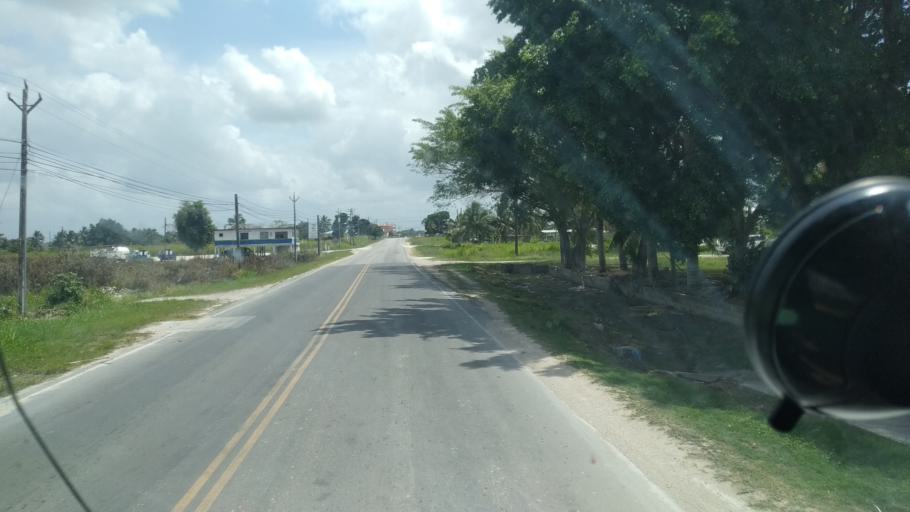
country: BZ
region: Orange Walk
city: Orange Walk
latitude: 18.0616
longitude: -88.5718
